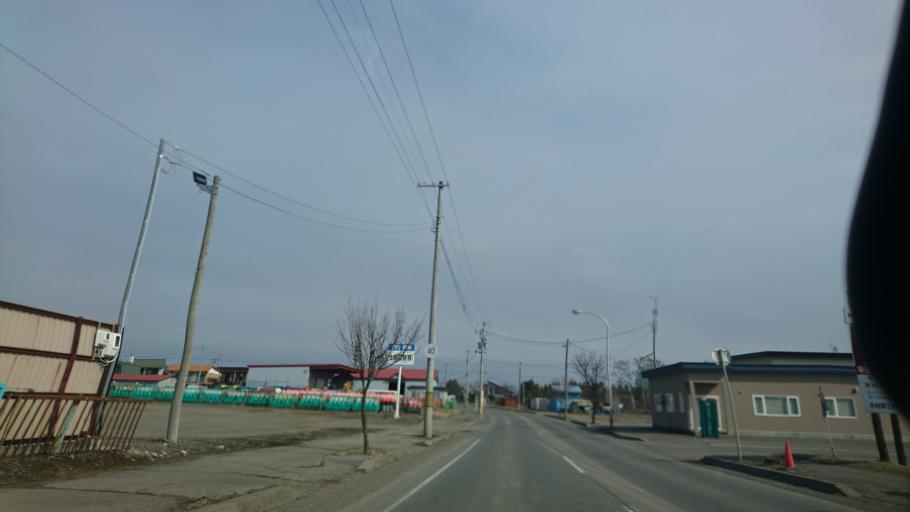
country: JP
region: Hokkaido
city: Obihiro
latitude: 42.9508
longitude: 143.2078
